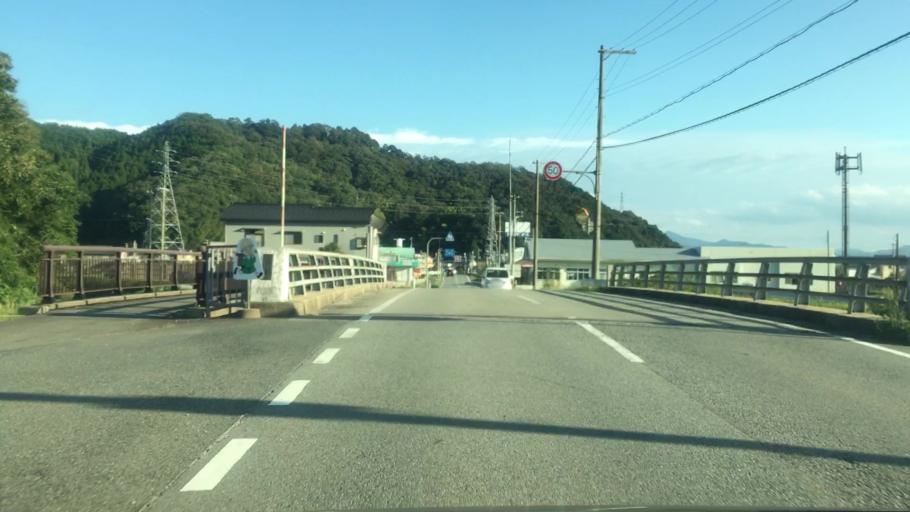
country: JP
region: Hyogo
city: Toyooka
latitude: 35.5608
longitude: 134.8230
